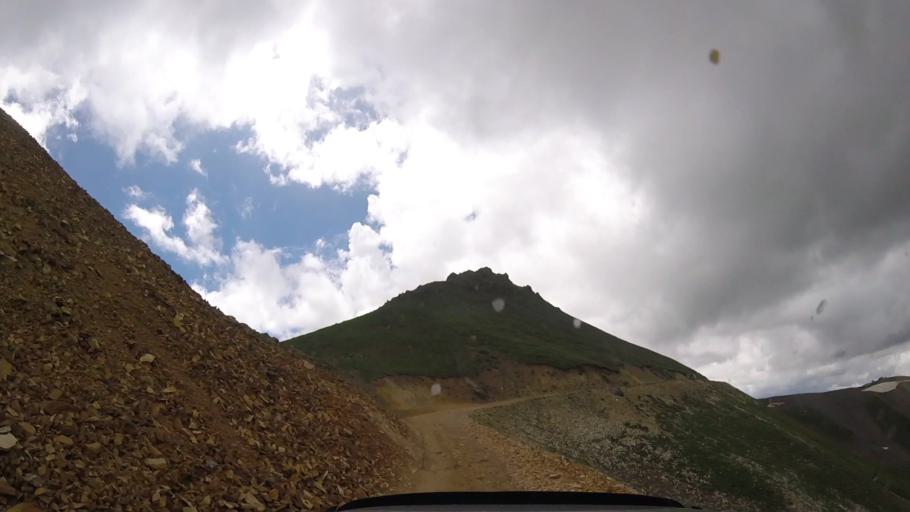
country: US
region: Colorado
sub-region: Ouray County
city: Ouray
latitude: 37.9723
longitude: -107.5879
